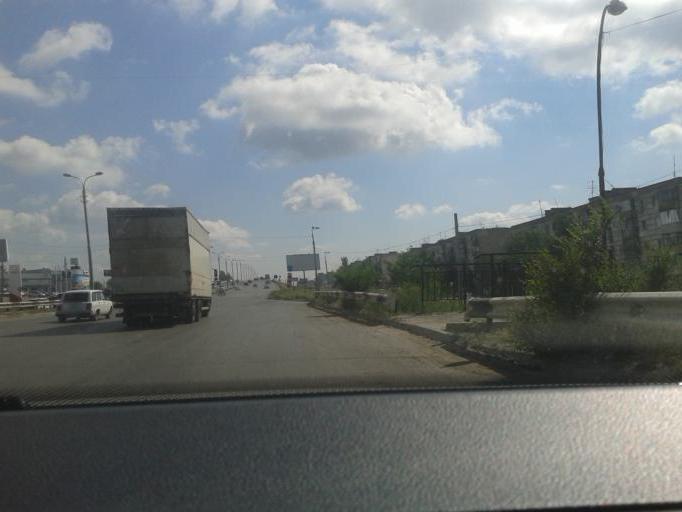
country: RU
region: Volgograd
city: Volgograd
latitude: 48.7520
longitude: 44.4758
